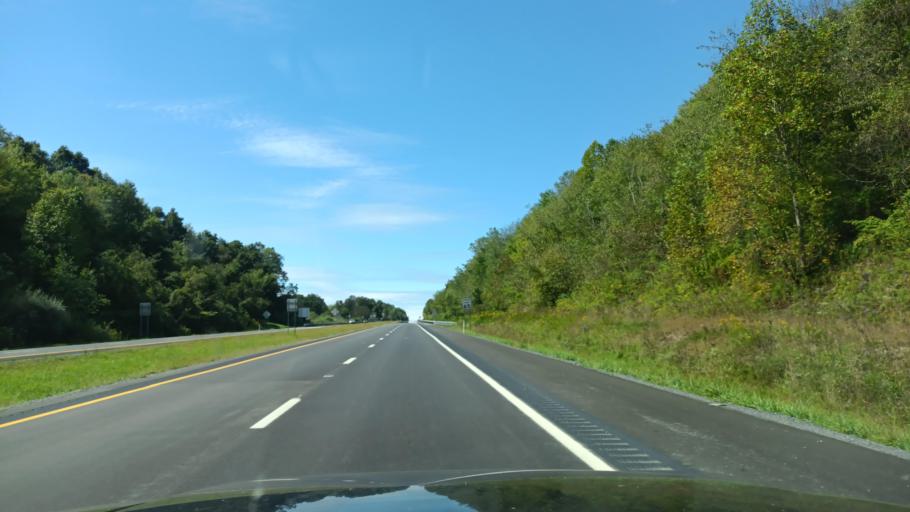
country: US
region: West Virginia
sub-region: Harrison County
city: Clarksburg
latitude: 39.2840
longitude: -80.4059
